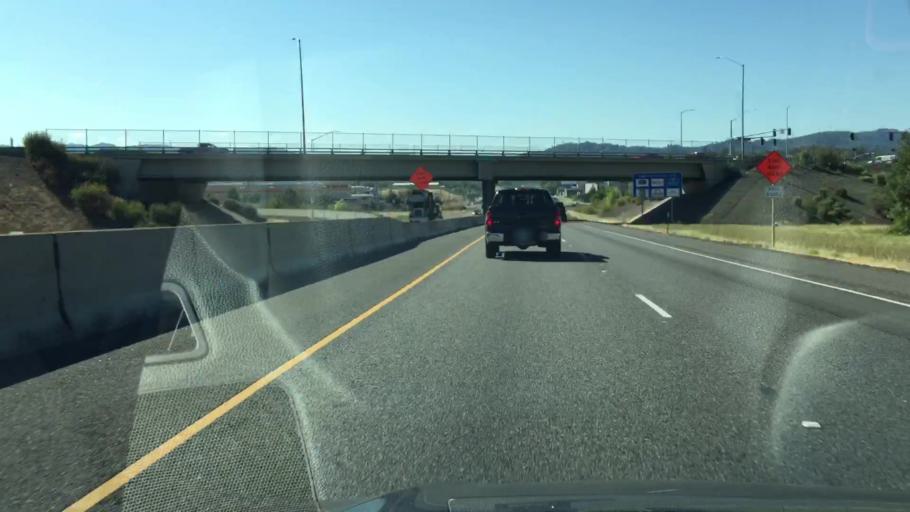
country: US
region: Oregon
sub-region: Douglas County
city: Roseburg
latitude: 43.2493
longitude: -123.3606
